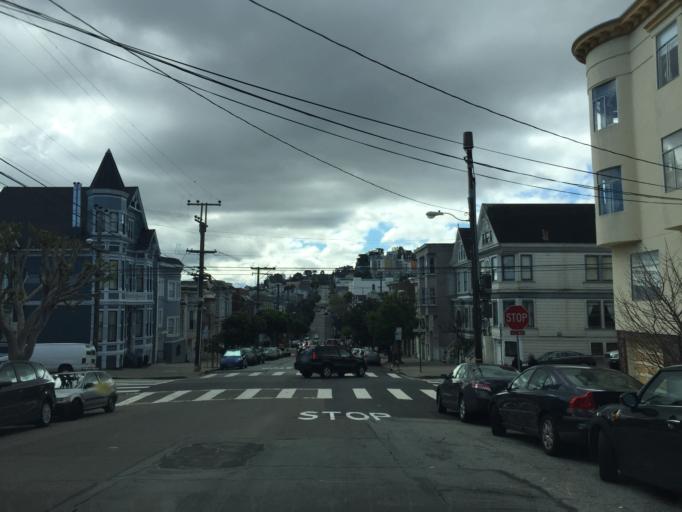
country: US
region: California
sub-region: San Francisco County
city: San Francisco
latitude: 37.7526
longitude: -122.4320
